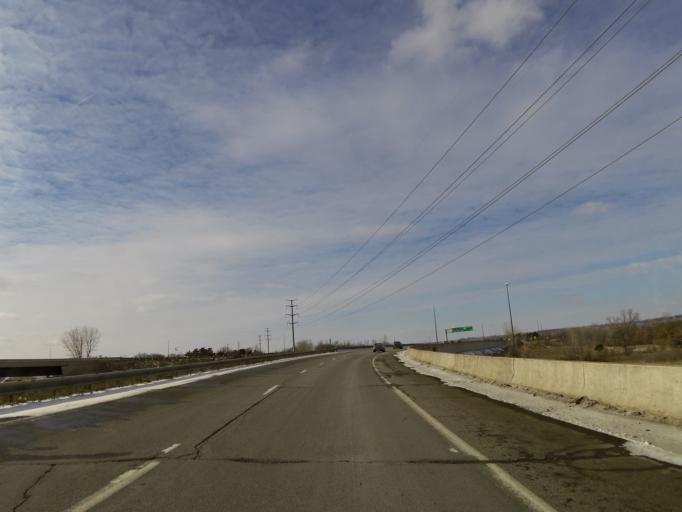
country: US
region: Minnesota
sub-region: Scott County
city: Savage
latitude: 44.7850
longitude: -93.3994
